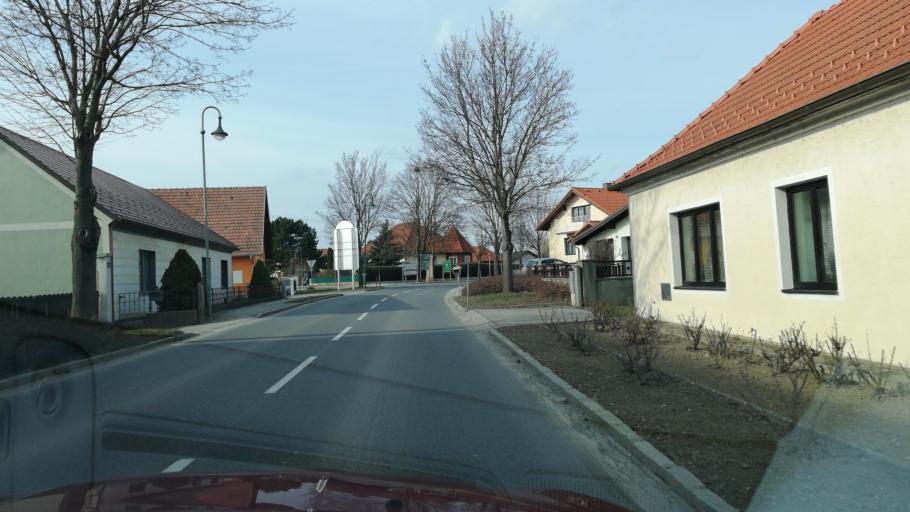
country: AT
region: Lower Austria
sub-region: Politischer Bezirk Tulln
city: Atzenbrugg
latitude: 48.3146
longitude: 15.8707
